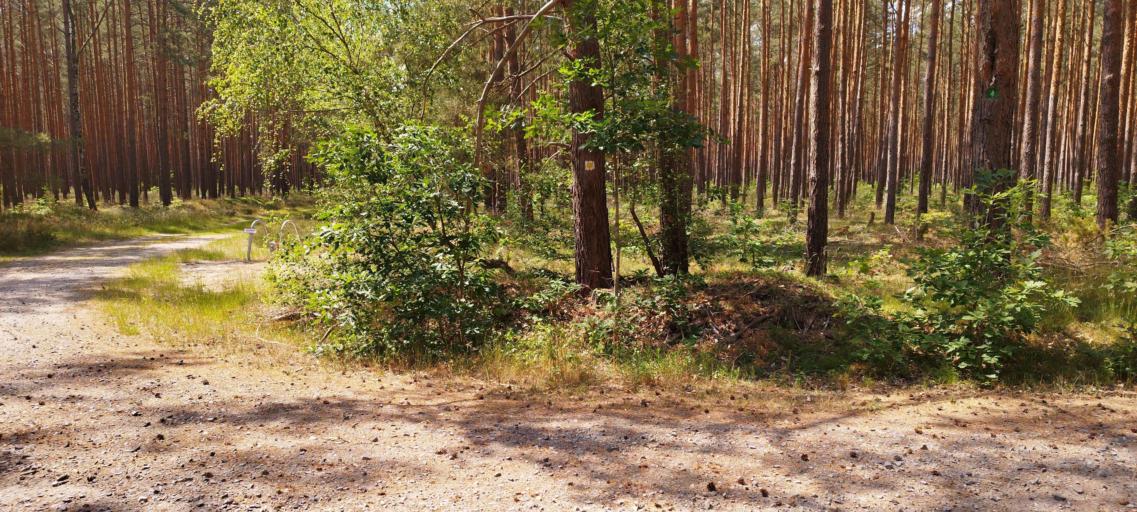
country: DE
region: Brandenburg
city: Rauen
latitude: 52.3505
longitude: 13.9897
